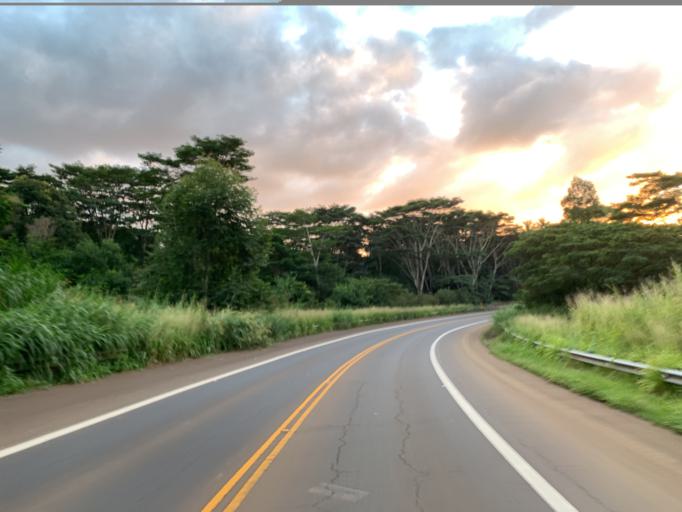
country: US
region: Hawaii
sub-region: Maui County
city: Haiku-Pauwela
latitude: 20.9193
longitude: -156.2957
